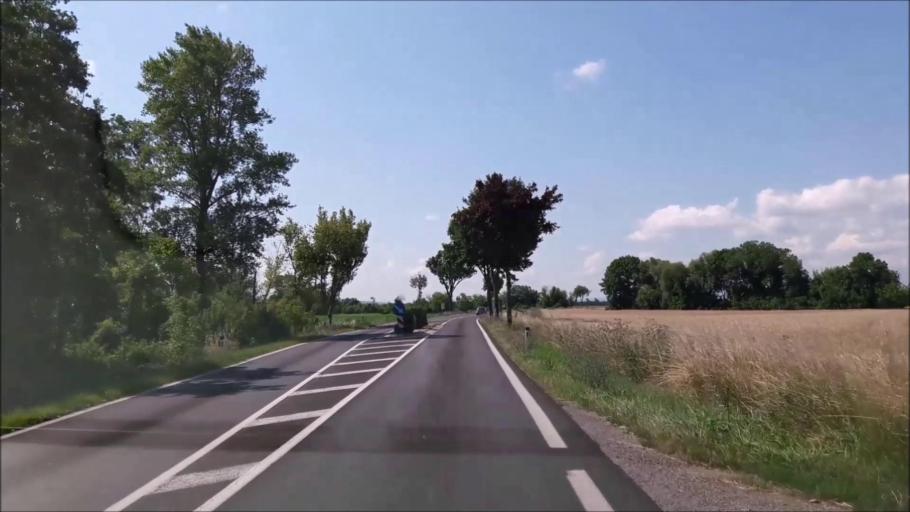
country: AT
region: Lower Austria
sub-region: Politischer Bezirk Wien-Umgebung
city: Moosbrunn
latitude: 48.0105
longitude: 16.4527
